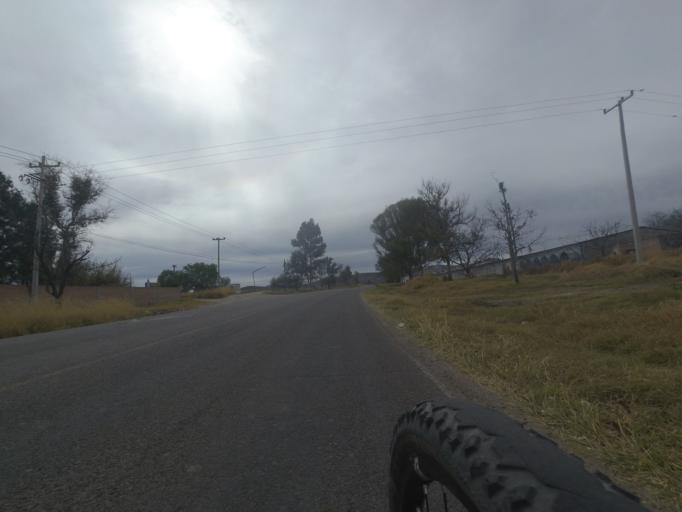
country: MX
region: Aguascalientes
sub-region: Aguascalientes
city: La Loma de los Negritos
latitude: 21.8373
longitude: -102.3571
